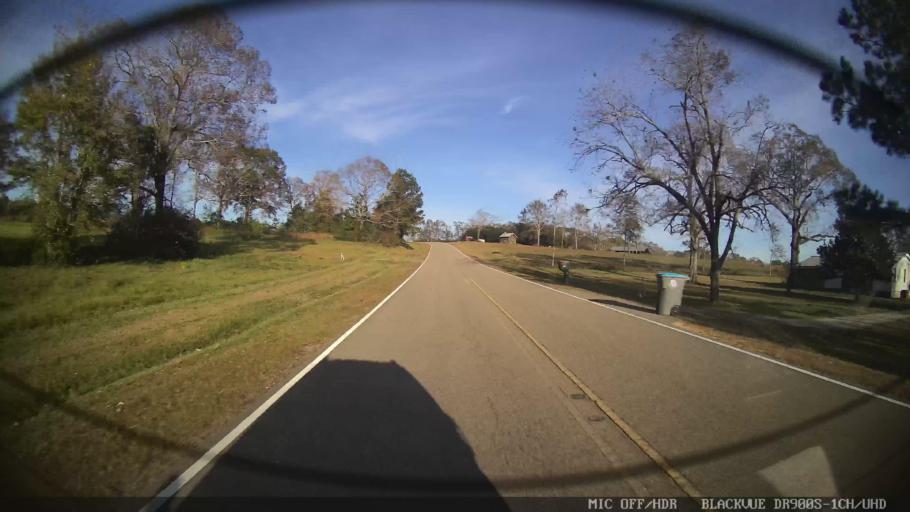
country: US
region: Mississippi
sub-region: Lamar County
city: Purvis
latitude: 31.1667
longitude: -89.3065
